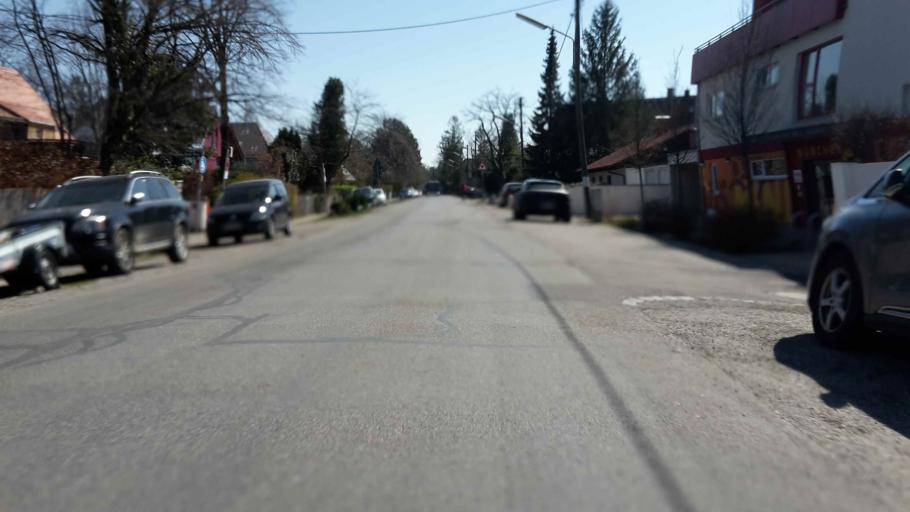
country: DE
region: Bavaria
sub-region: Upper Bavaria
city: Pasing
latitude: 48.1735
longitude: 11.4777
